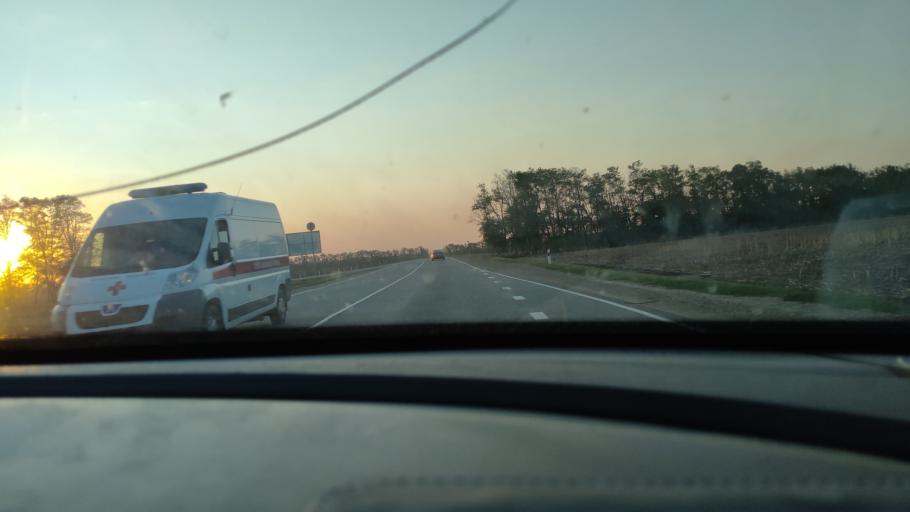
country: RU
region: Krasnodarskiy
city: Starominskaya
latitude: 46.4940
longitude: 39.0568
